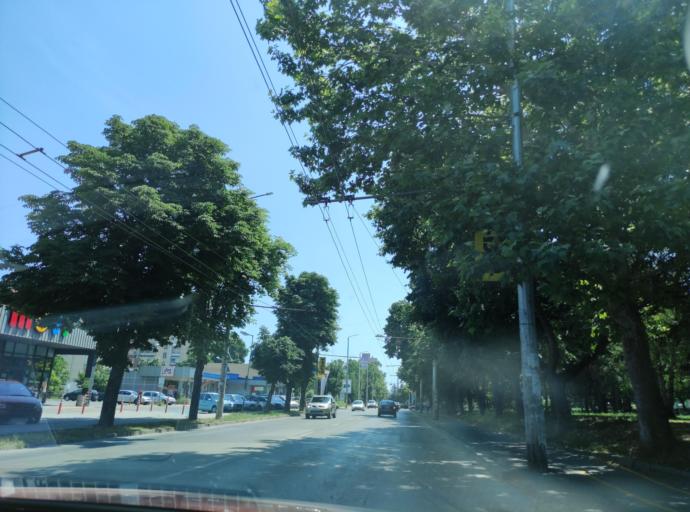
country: BG
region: Pleven
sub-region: Obshtina Pleven
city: Pleven
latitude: 43.4239
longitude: 24.5951
